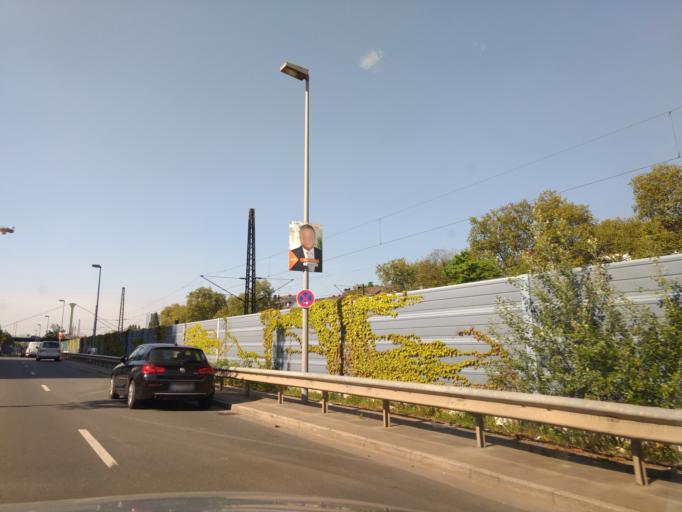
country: DE
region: North Rhine-Westphalia
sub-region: Regierungsbezirk Dusseldorf
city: Dusseldorf
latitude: 51.2333
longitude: 6.7966
